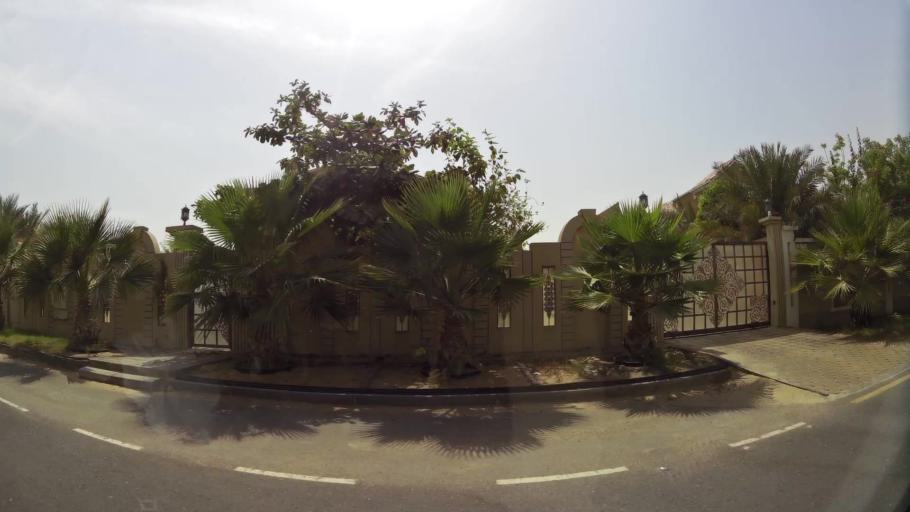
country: AE
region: Ash Shariqah
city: Sharjah
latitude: 25.2485
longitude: 55.4946
